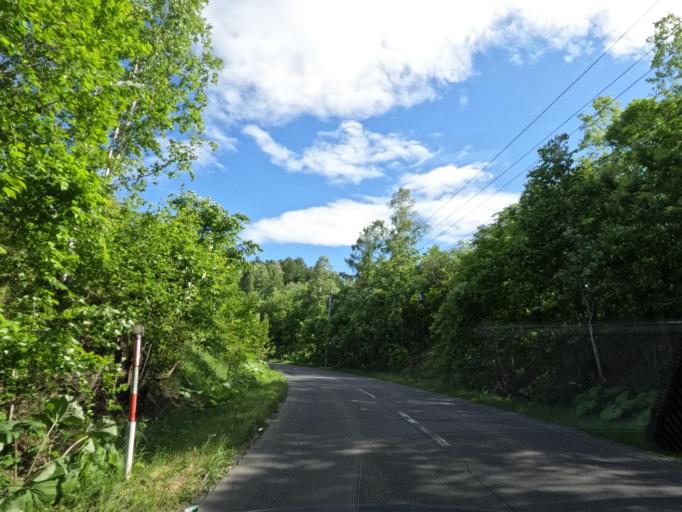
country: JP
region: Hokkaido
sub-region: Asahikawa-shi
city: Asahikawa
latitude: 43.7403
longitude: 142.5330
